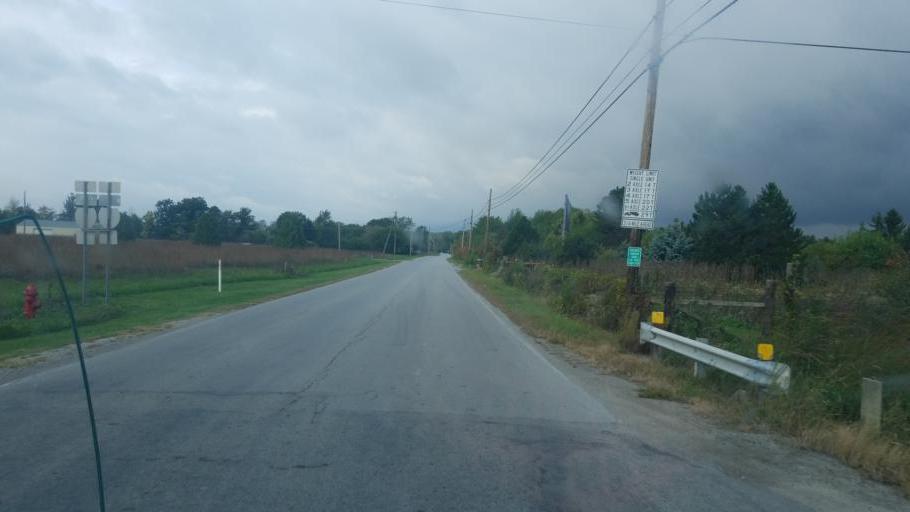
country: US
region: Ohio
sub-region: Wood County
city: North Baltimore
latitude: 41.1824
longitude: -83.6513
